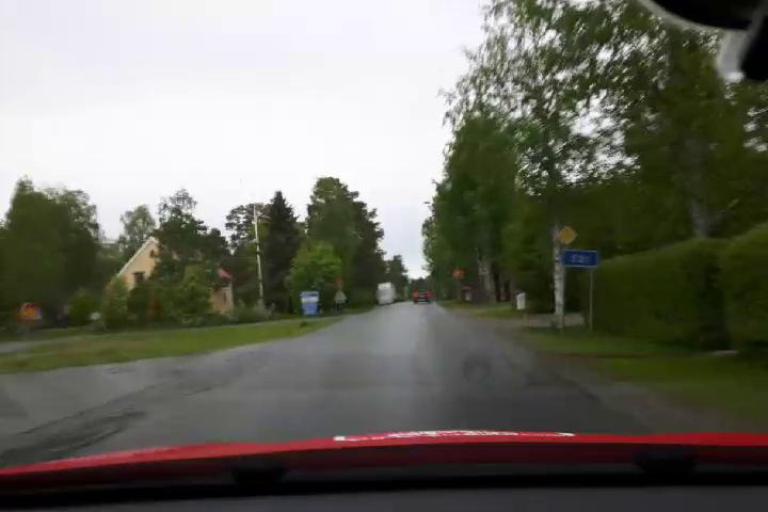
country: SE
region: Jaemtland
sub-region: Bergs Kommun
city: Hoverberg
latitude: 62.7686
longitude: 14.4283
